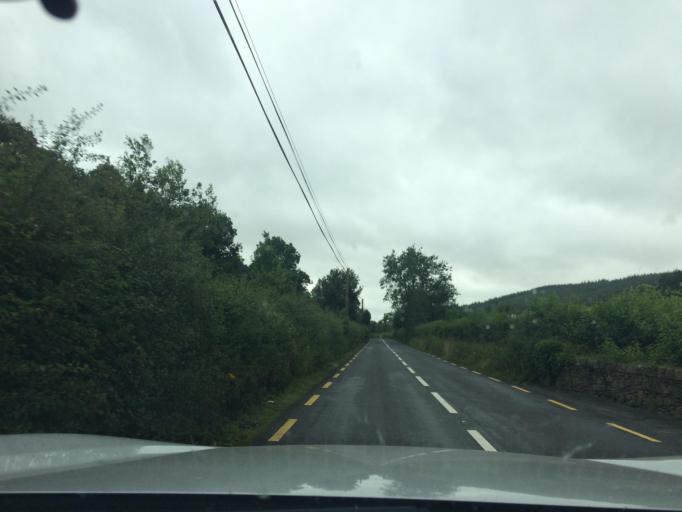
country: IE
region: Munster
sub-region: South Tipperary
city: Cluain Meala
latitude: 52.3285
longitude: -7.7365
